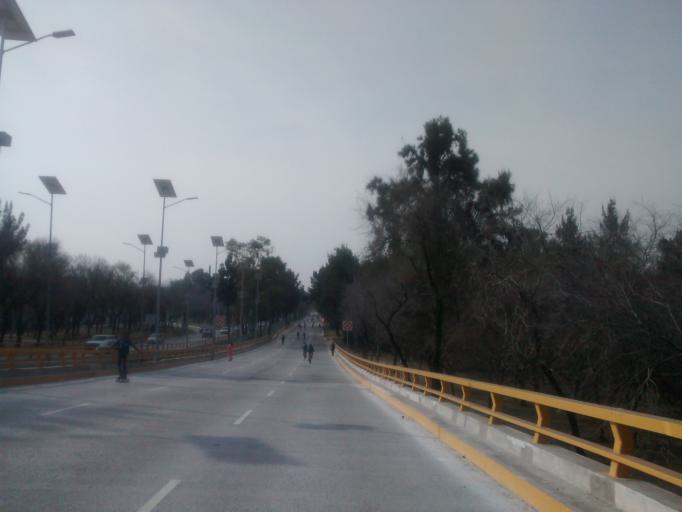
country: MX
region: Mexico City
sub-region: Iztacalco
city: Iztacalco
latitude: 19.3948
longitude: -99.0992
